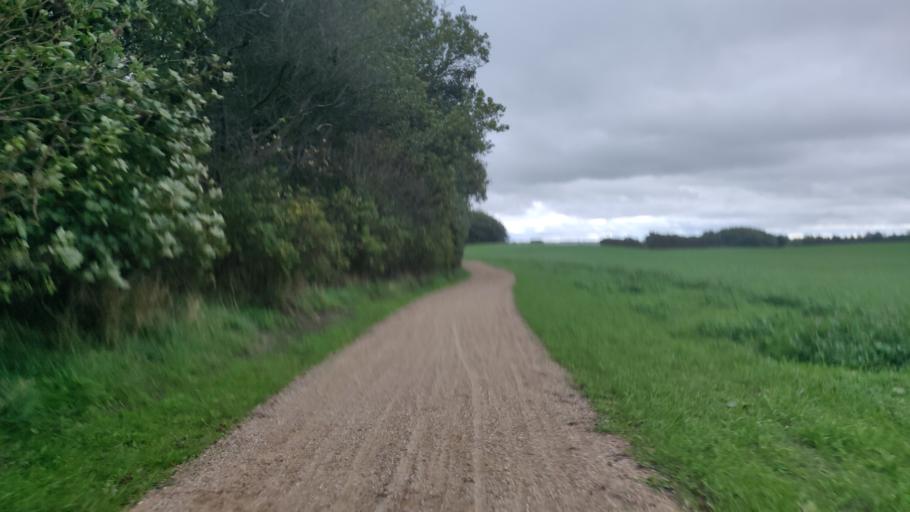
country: DK
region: South Denmark
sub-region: Kolding Kommune
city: Lunderskov
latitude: 55.5435
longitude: 9.3329
